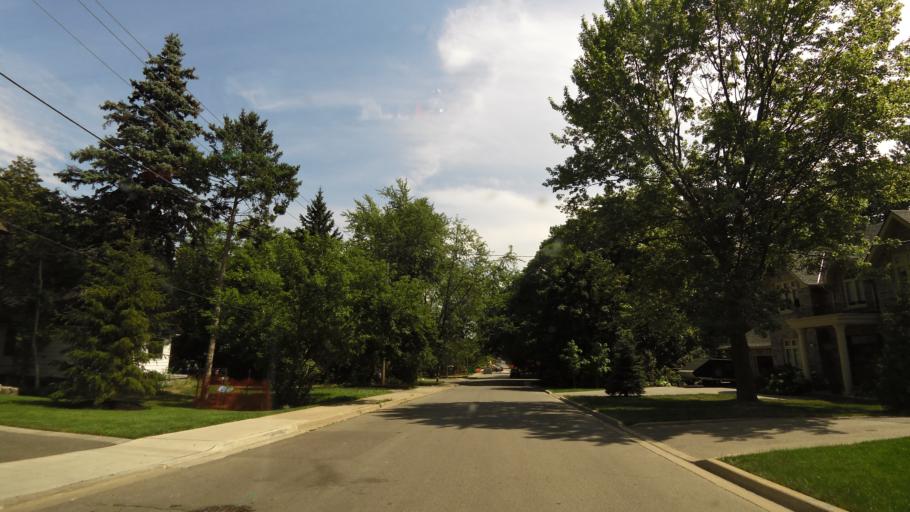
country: CA
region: Ontario
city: Mississauga
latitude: 43.5733
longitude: -79.5853
